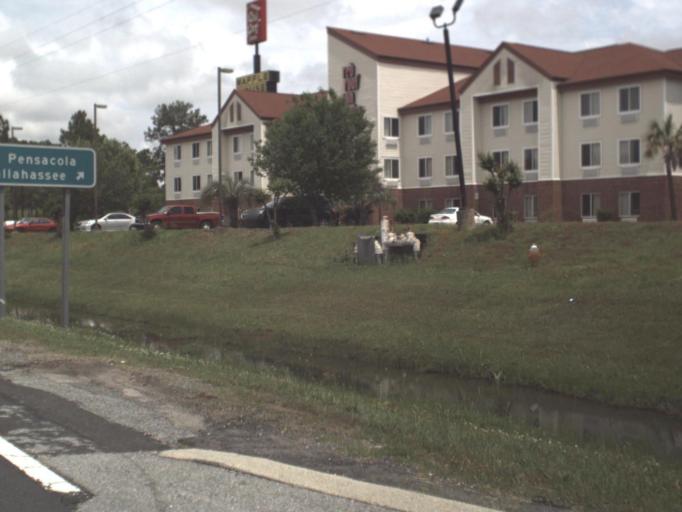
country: US
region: Florida
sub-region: Santa Rosa County
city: Bagdad
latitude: 30.5318
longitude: -87.0872
